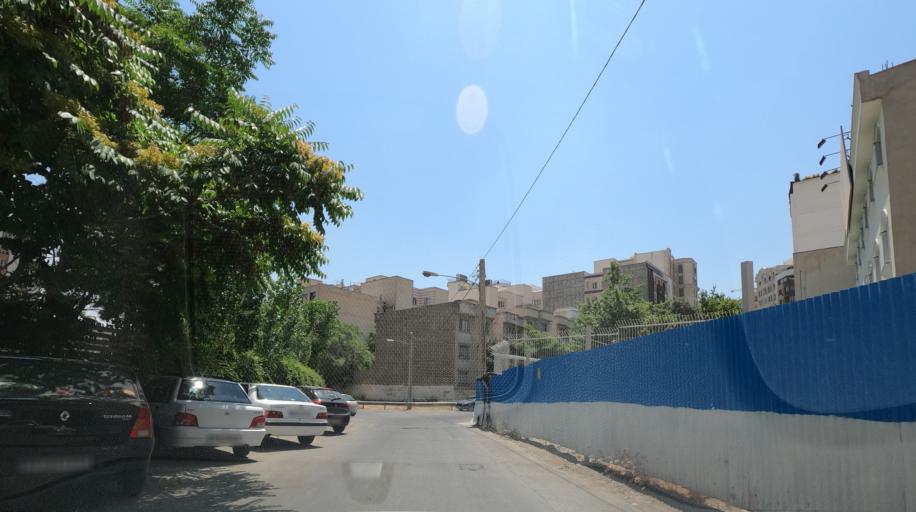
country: IR
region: Tehran
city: Tajrish
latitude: 35.7884
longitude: 51.3850
